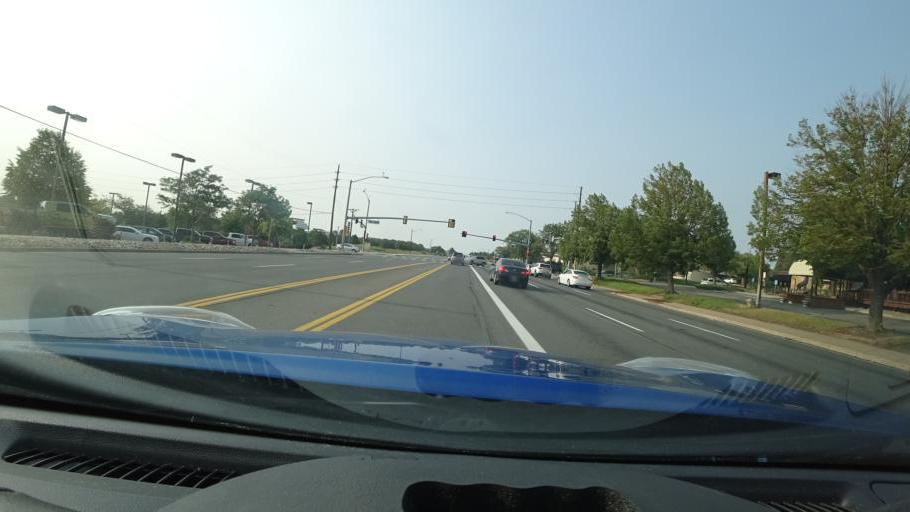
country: US
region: Colorado
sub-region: Adams County
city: Aurora
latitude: 39.6668
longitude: -104.8661
